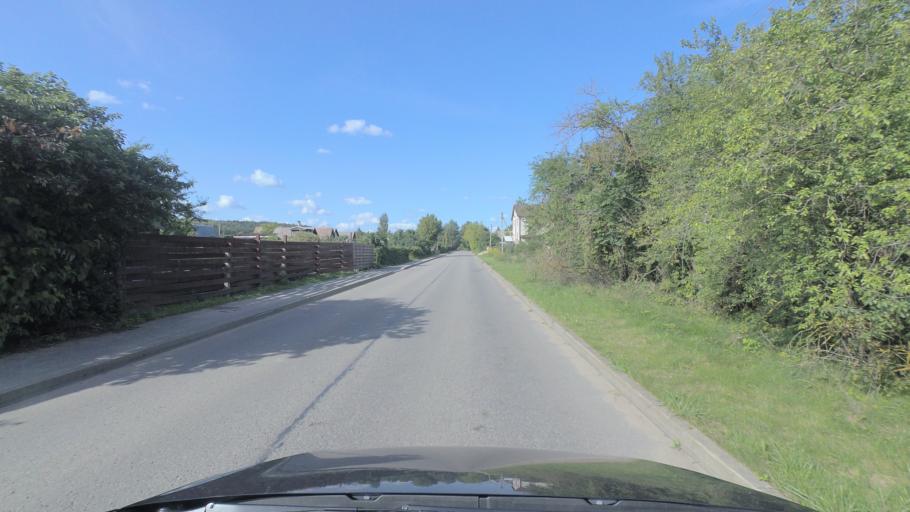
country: LT
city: Nemencine
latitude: 54.8343
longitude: 25.3691
